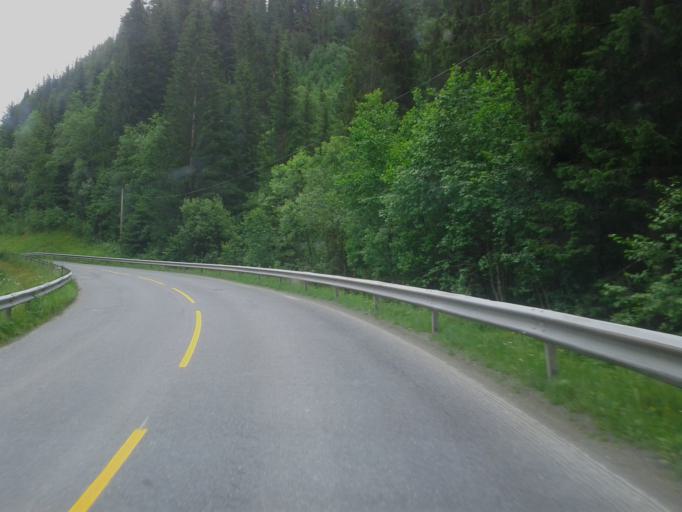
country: NO
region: Sor-Trondelag
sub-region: Midtre Gauldal
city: Storen
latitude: 62.9924
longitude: 10.4759
